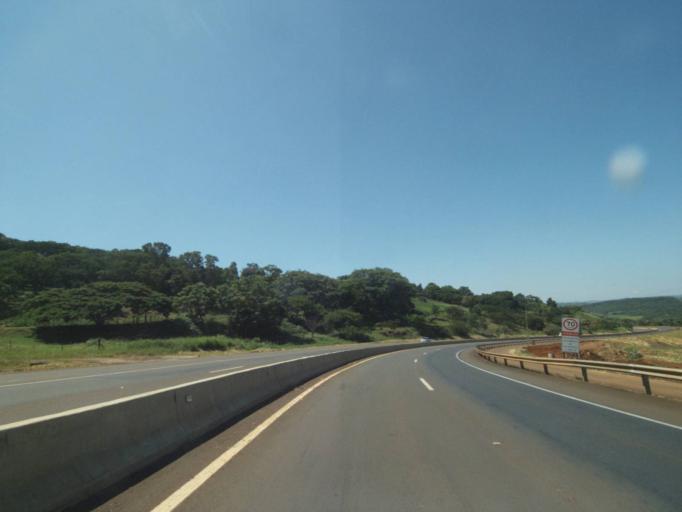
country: BR
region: Parana
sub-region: Londrina
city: Londrina
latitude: -23.3820
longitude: -51.1342
